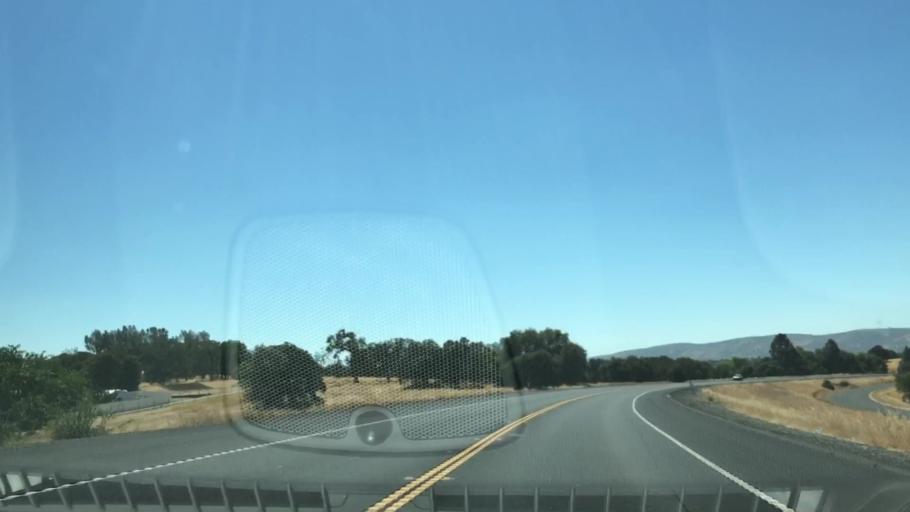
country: US
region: California
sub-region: Calaveras County
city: Copperopolis
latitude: 37.9827
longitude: -120.6458
